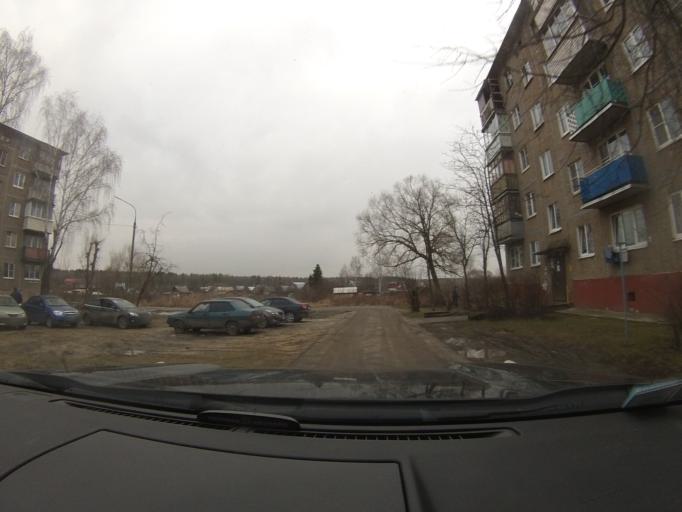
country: RU
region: Moskovskaya
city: Lopatinskiy
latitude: 55.3447
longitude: 38.7230
